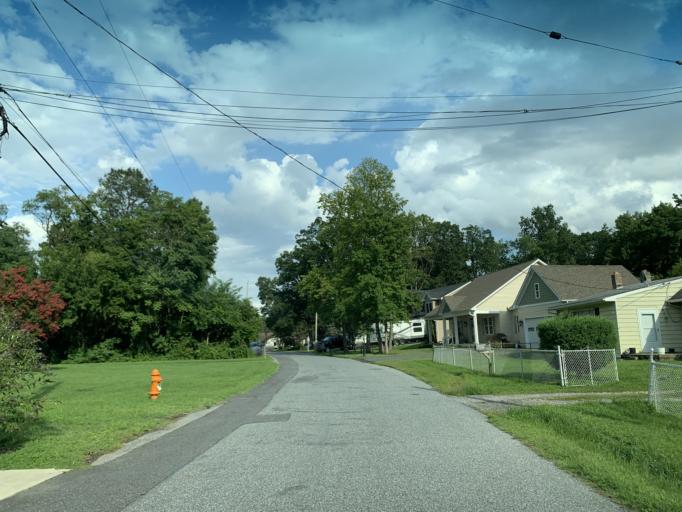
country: US
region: Maryland
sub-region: Baltimore County
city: Essex
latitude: 39.2903
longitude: -76.4385
